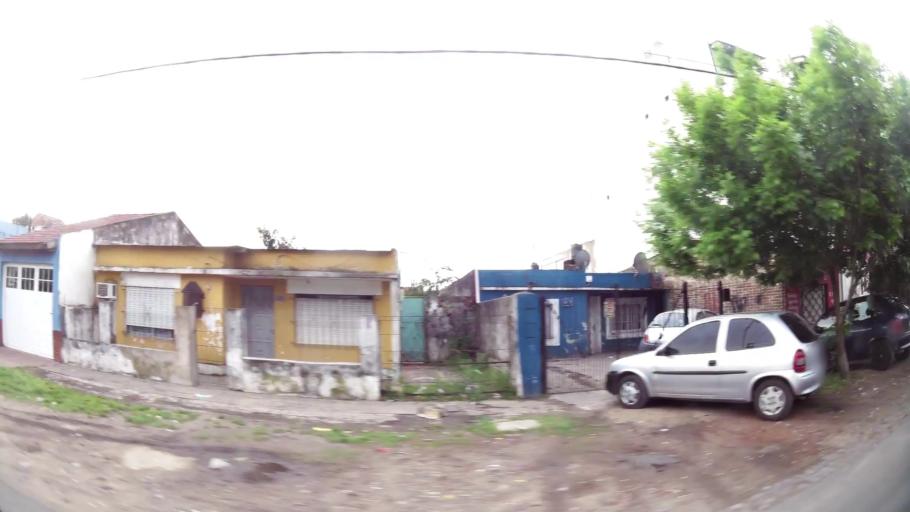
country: AR
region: Buenos Aires
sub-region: Partido de Lanus
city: Lanus
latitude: -34.7320
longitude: -58.3429
